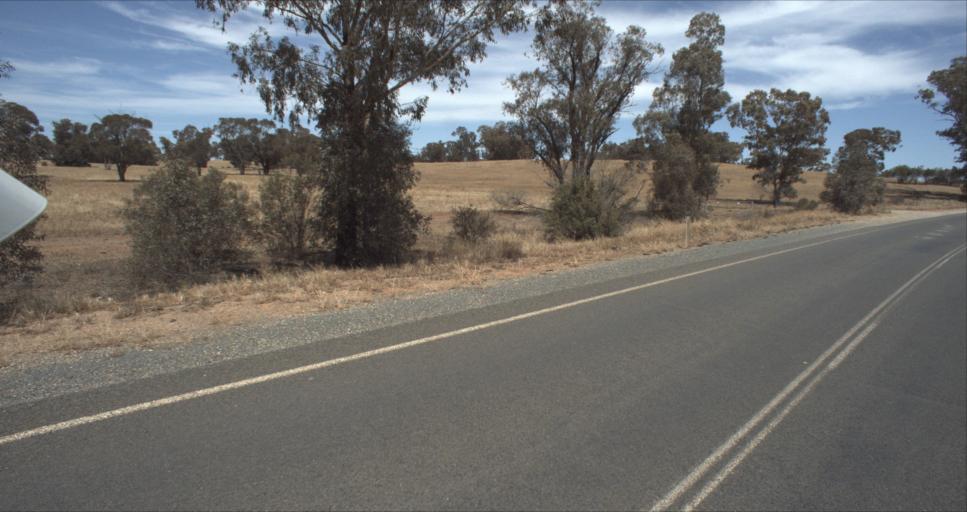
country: AU
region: New South Wales
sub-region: Leeton
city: Leeton
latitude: -34.6589
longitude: 146.4565
